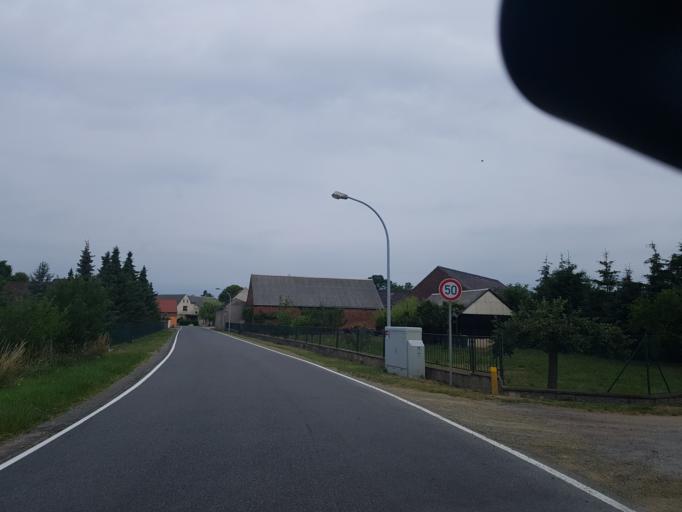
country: DE
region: Brandenburg
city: Schonewalde
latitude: 51.7016
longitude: 13.6037
